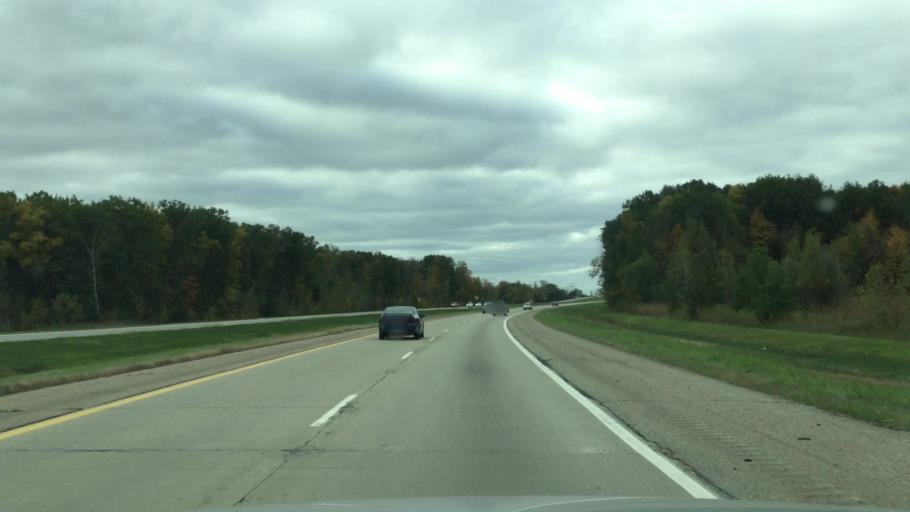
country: US
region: Michigan
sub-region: Macomb County
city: Romeo
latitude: 42.7958
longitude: -83.0011
